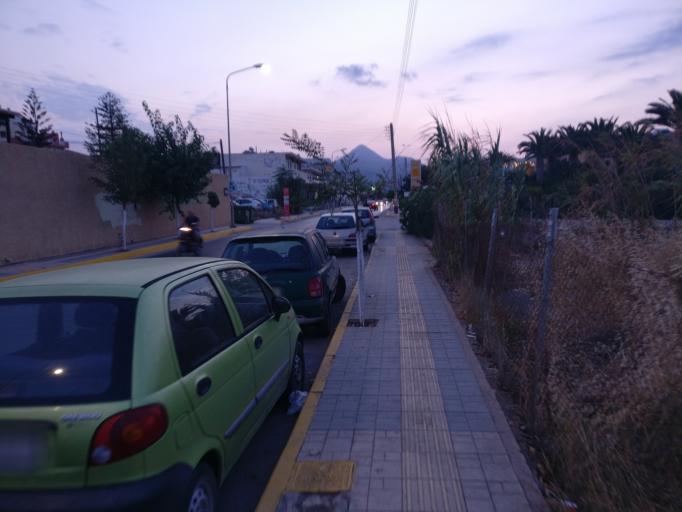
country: GR
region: Crete
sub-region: Nomos Irakleiou
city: Gazi
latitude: 35.3355
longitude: 25.0861
